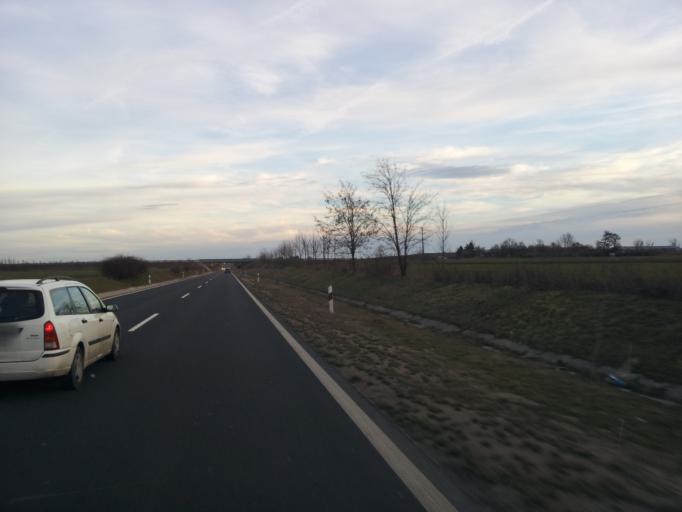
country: HU
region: Veszprem
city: Balatonkenese
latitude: 47.0764
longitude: 18.0689
